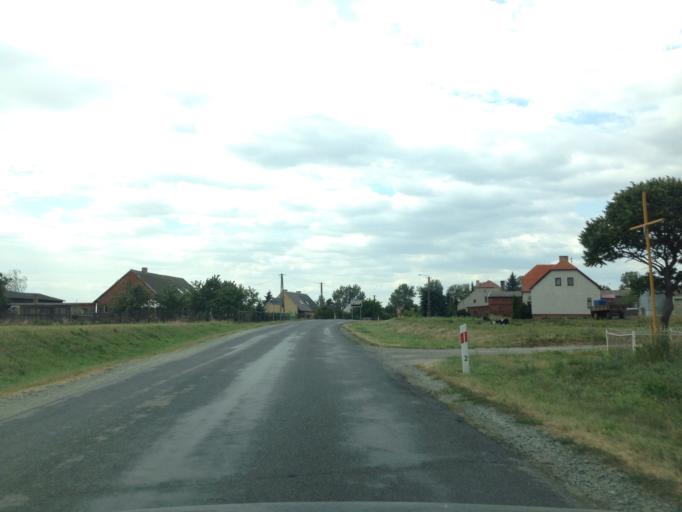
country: PL
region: Kujawsko-Pomorskie
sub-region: Powiat wabrzeski
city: Pluznica
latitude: 53.2060
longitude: 18.7876
